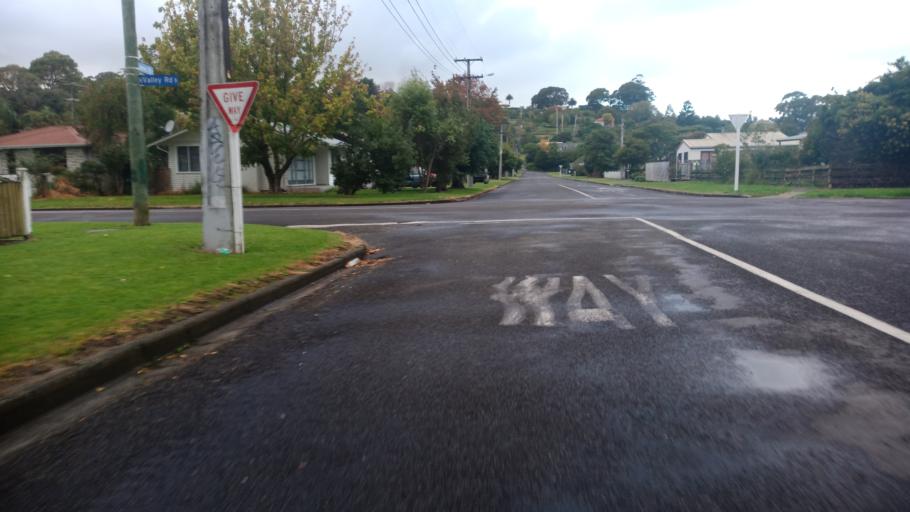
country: NZ
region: Gisborne
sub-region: Gisborne District
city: Gisborne
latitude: -38.6388
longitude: 178.0110
